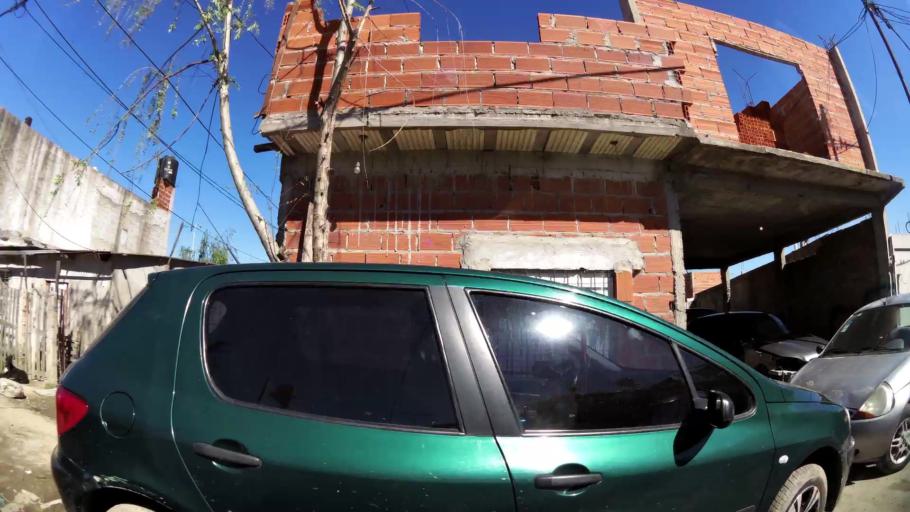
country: AR
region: Buenos Aires
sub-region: Partido de Quilmes
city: Quilmes
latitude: -34.7048
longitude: -58.3034
